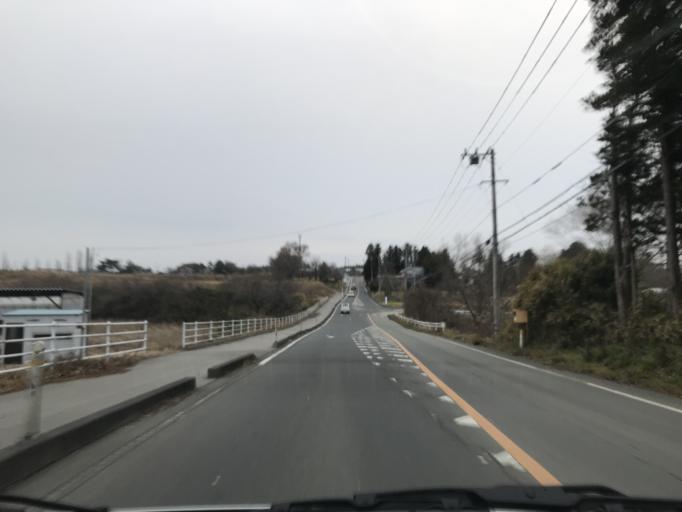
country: JP
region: Miyagi
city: Wakuya
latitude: 38.6749
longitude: 141.1113
